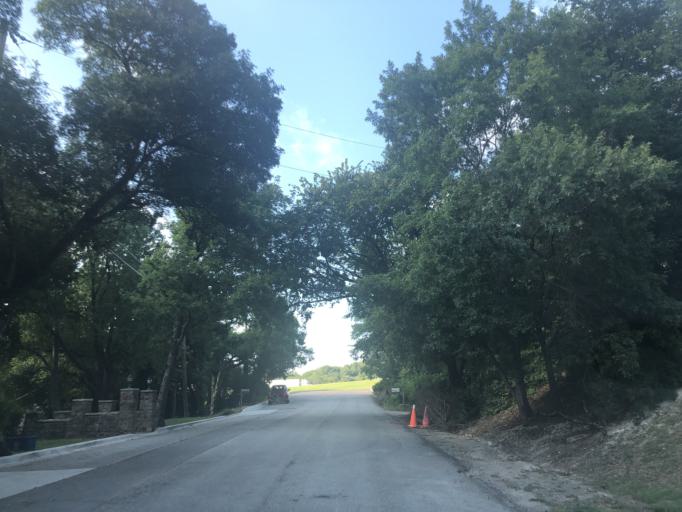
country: US
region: Texas
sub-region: Dallas County
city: Duncanville
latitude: 32.6713
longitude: -96.9236
